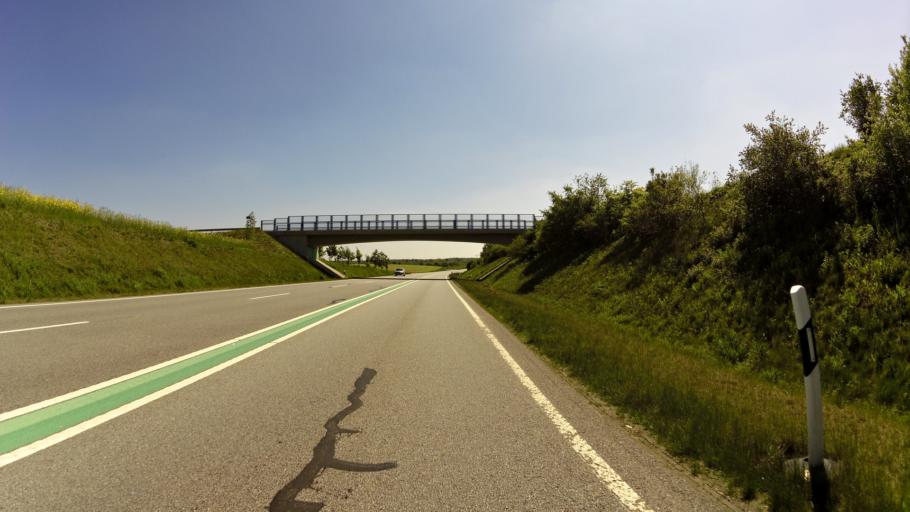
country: DE
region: Saxony
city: Radeberg
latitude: 51.0840
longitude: 13.9376
